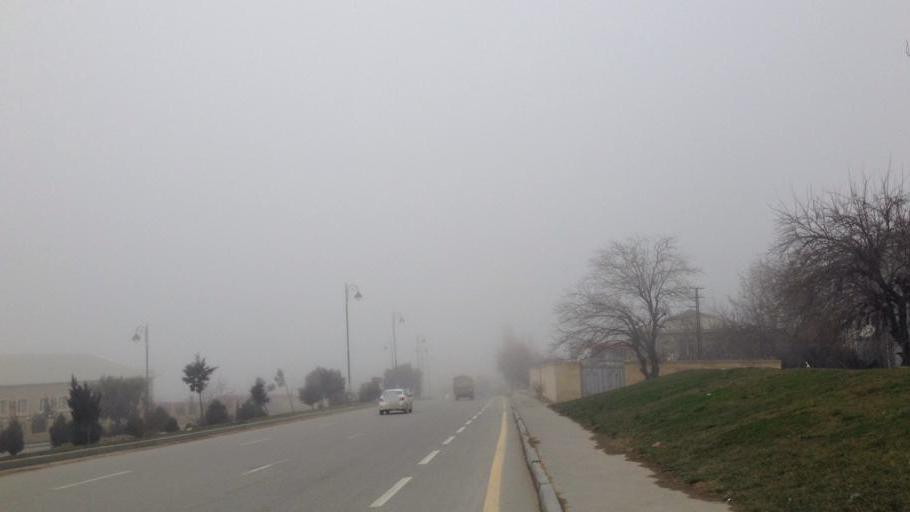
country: AZ
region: Baki
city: Qaracuxur
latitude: 40.3507
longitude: 49.9600
